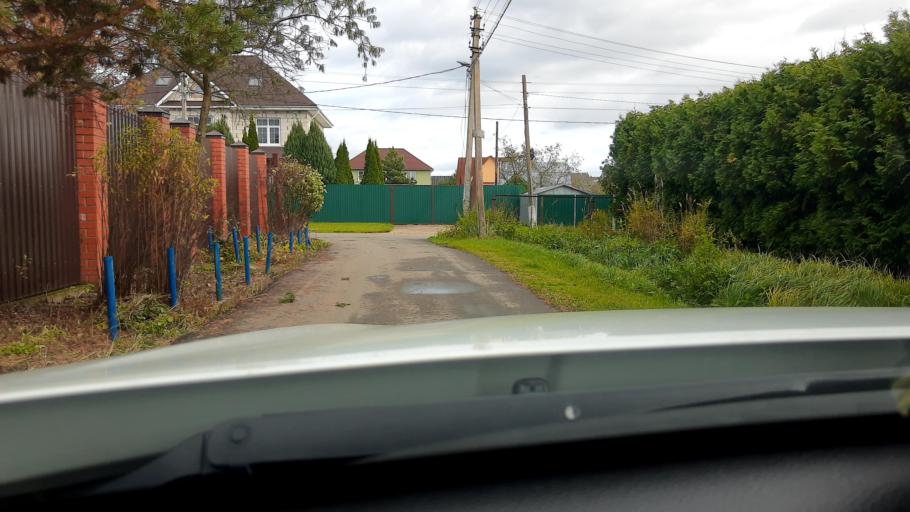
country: RU
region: Moskovskaya
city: Selyatino
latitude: 55.4526
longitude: 36.9494
